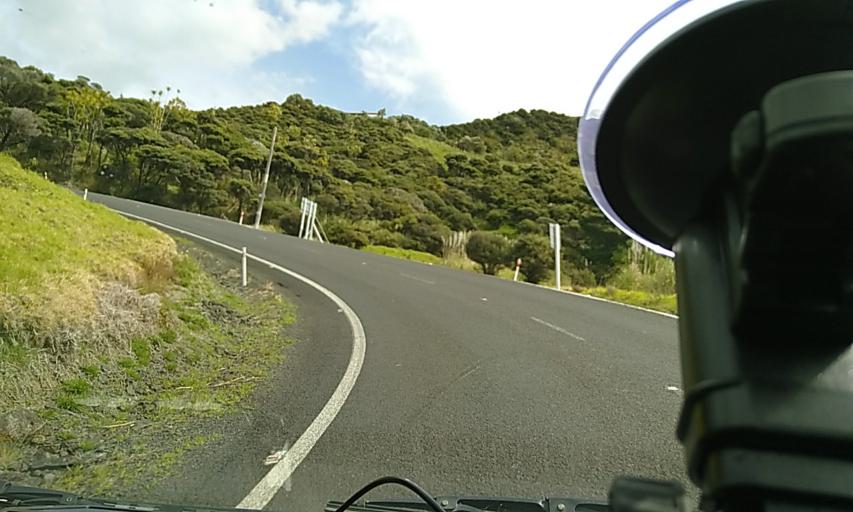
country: NZ
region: Northland
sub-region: Far North District
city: Ahipara
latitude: -35.5398
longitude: 173.3849
